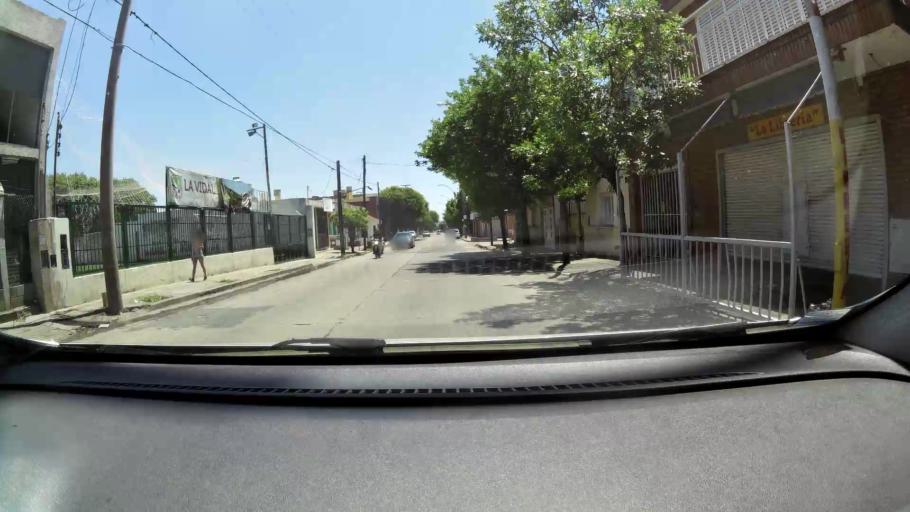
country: AR
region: Cordoba
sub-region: Departamento de Capital
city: Cordoba
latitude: -31.4124
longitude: -64.2255
